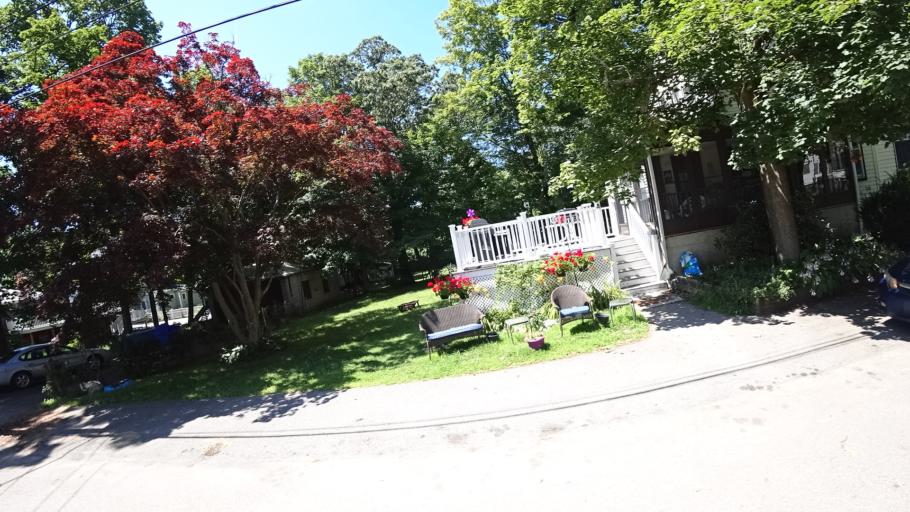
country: US
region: Massachusetts
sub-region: Norfolk County
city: Dedham
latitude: 42.2357
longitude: -71.1605
